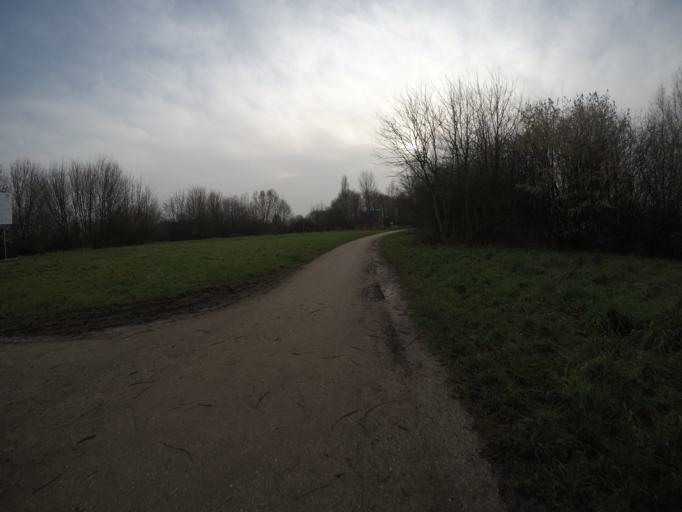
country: DE
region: North Rhine-Westphalia
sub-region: Regierungsbezirk Dusseldorf
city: Xanten
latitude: 51.6796
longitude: 6.4562
